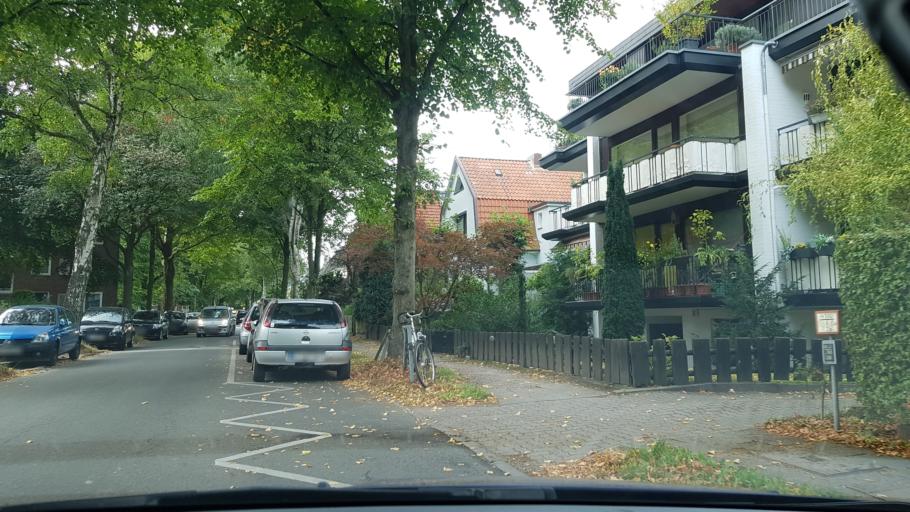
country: DE
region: Hamburg
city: Steilshoop
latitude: 53.6016
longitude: 10.0548
